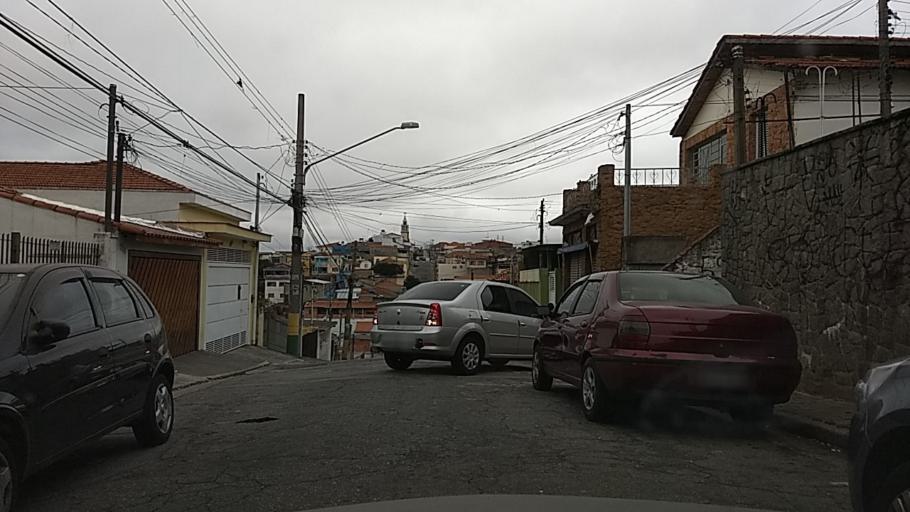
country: BR
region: Sao Paulo
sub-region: Guarulhos
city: Guarulhos
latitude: -23.4920
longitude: -46.5953
